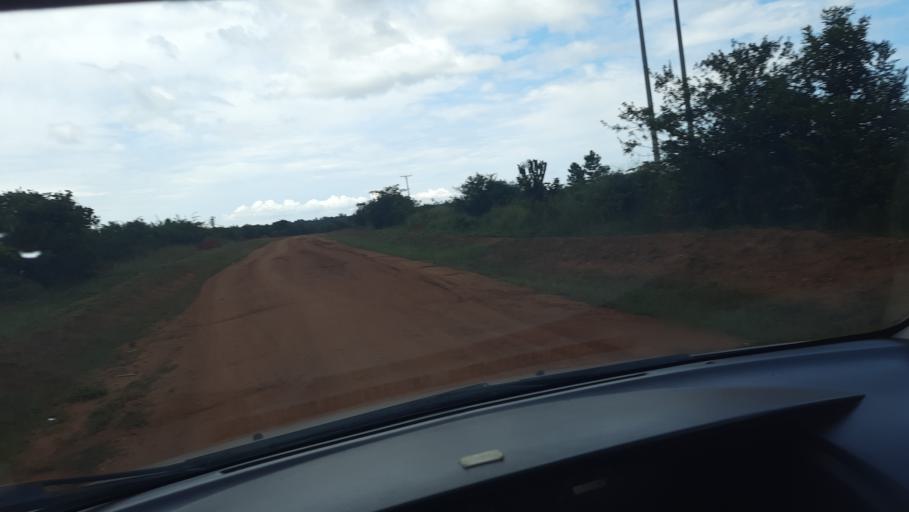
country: UG
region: Central Region
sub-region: Nakasongola District
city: Nakasongola
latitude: 1.3732
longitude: 32.4837
